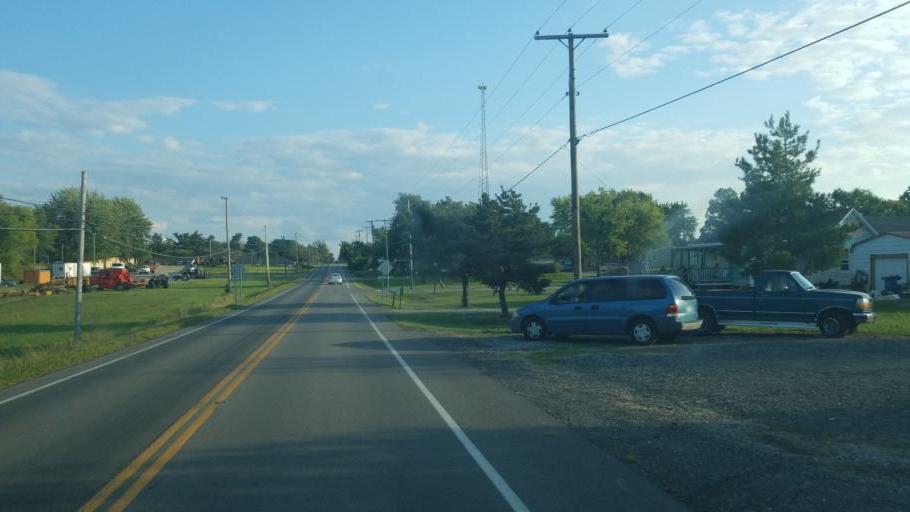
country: US
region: Ohio
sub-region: Huron County
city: Willard
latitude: 41.0672
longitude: -82.7167
